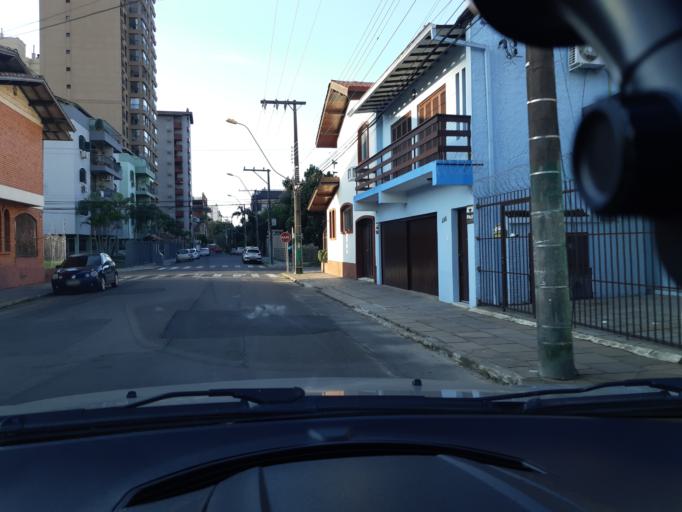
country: BR
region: Rio Grande do Sul
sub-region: Sao Leopoldo
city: Sao Leopoldo
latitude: -29.7643
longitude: -51.1420
